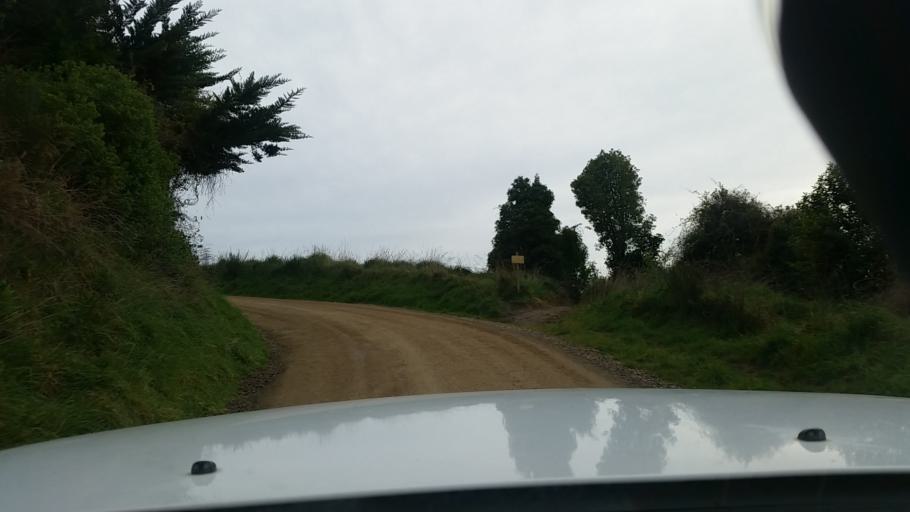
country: NZ
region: Canterbury
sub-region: Christchurch City
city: Christchurch
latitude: -43.6342
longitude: 172.7344
